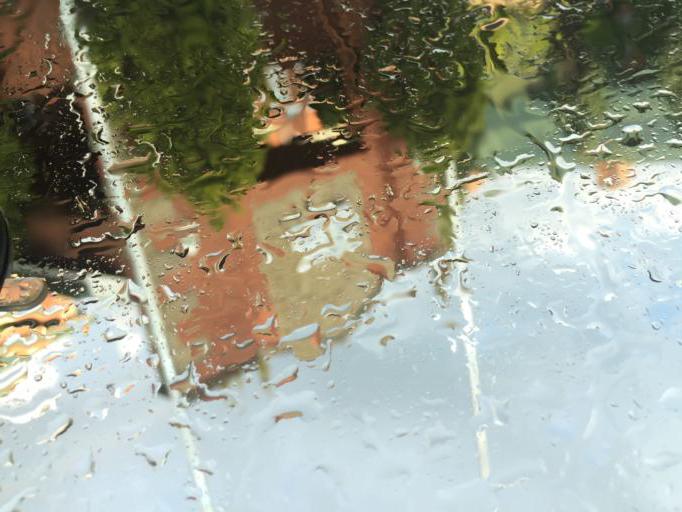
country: LS
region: Maseru
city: Nako
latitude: -29.4785
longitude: 28.0619
